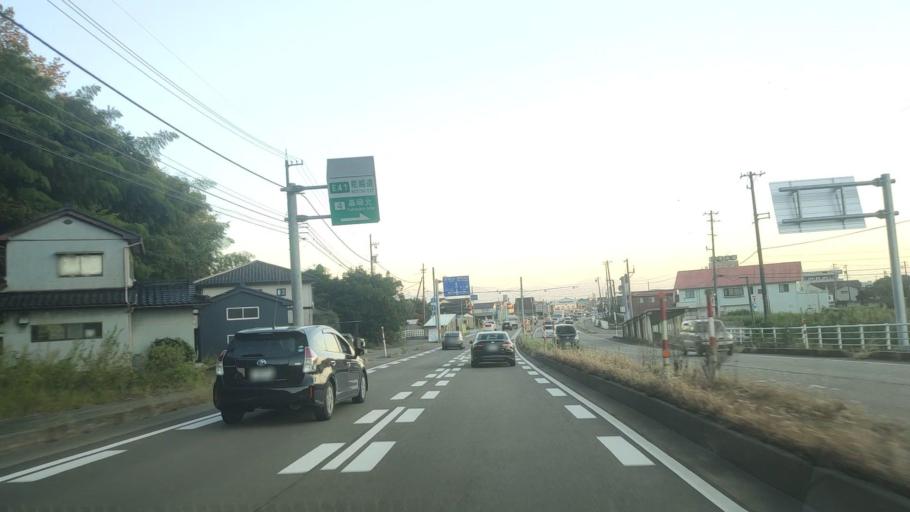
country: JP
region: Toyama
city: Takaoka
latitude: 36.7805
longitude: 137.0001
